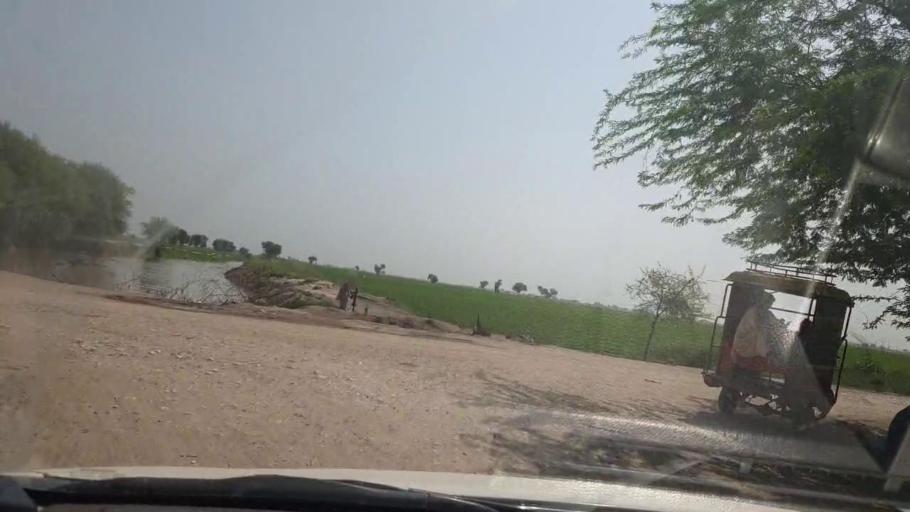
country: PK
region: Sindh
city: Chak
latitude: 27.8946
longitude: 68.7976
